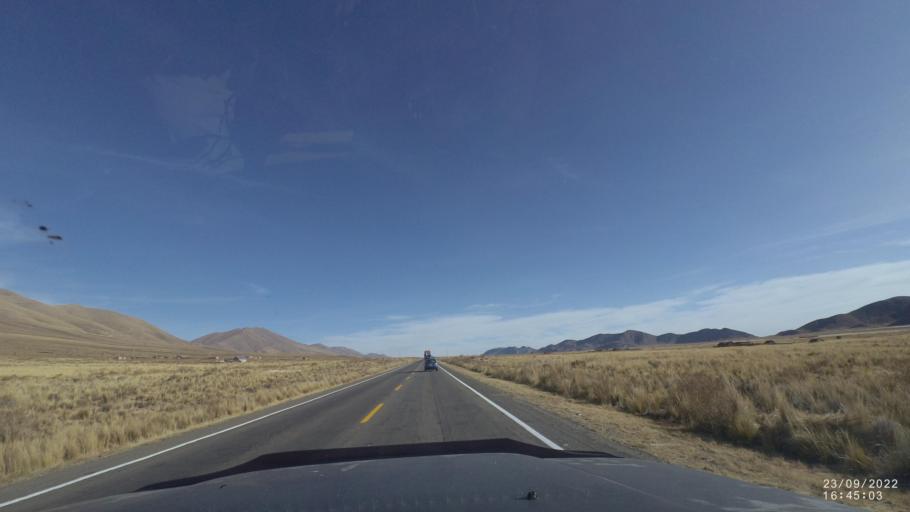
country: BO
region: Oruro
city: Poopo
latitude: -18.3367
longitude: -66.9866
